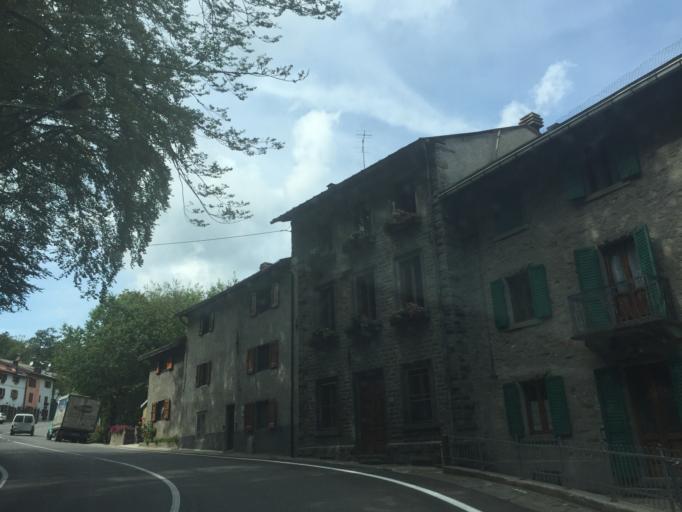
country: IT
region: Tuscany
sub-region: Provincia di Pistoia
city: Abetone
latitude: 44.1377
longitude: 10.6772
